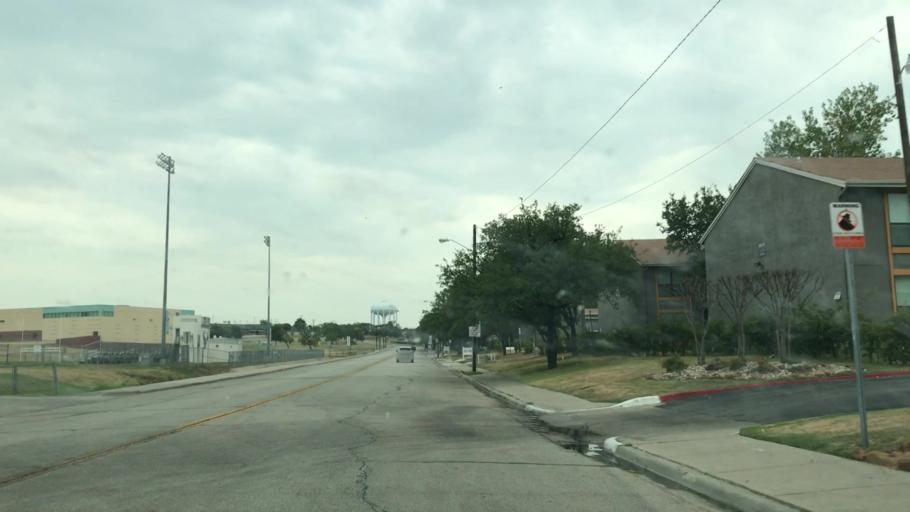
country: US
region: Texas
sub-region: Dallas County
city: Irving
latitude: 32.8638
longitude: -96.9886
